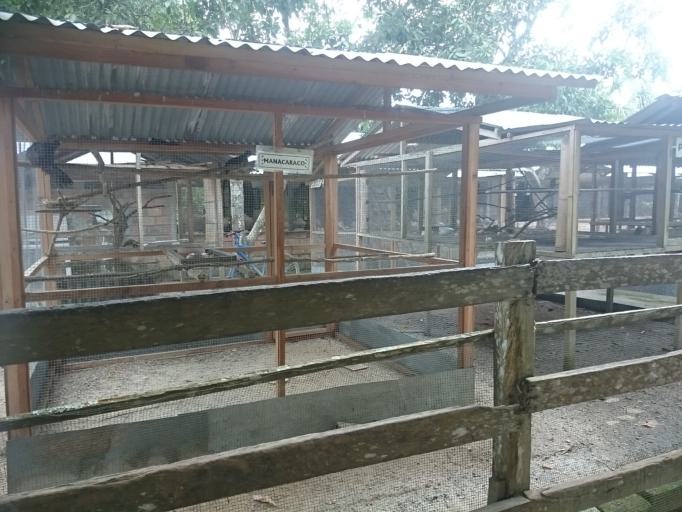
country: PE
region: San Martin
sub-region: Provincia de Rioja
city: Rioja
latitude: -6.0560
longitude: -77.1768
